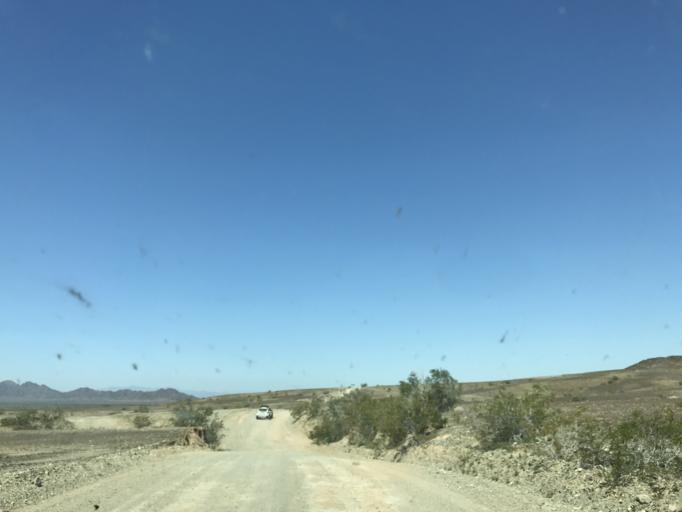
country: US
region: California
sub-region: Riverside County
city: Mesa Verde
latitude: 33.4981
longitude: -114.8471
